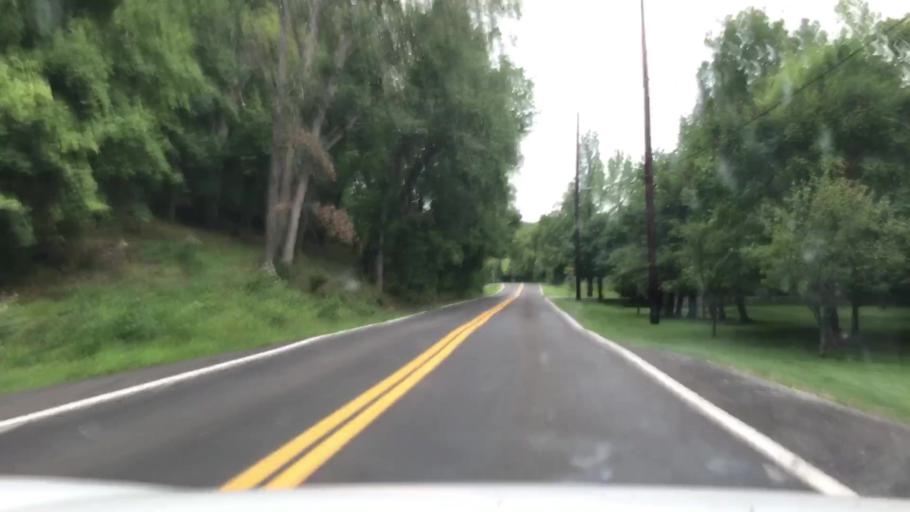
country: US
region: Missouri
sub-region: Saint Louis County
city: Clarkson Valley
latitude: 38.6406
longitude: -90.6113
